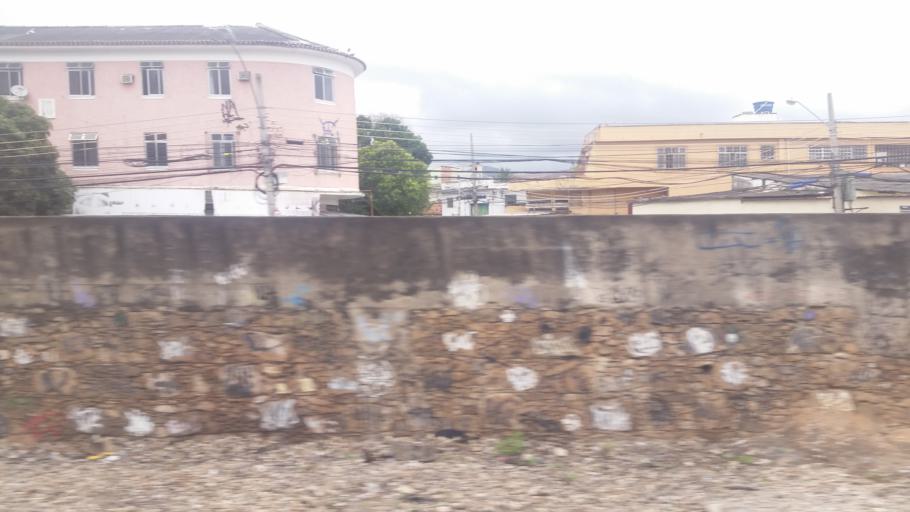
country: BR
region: Rio de Janeiro
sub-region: Sao Joao De Meriti
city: Sao Joao de Meriti
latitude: -22.8680
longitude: -43.3522
